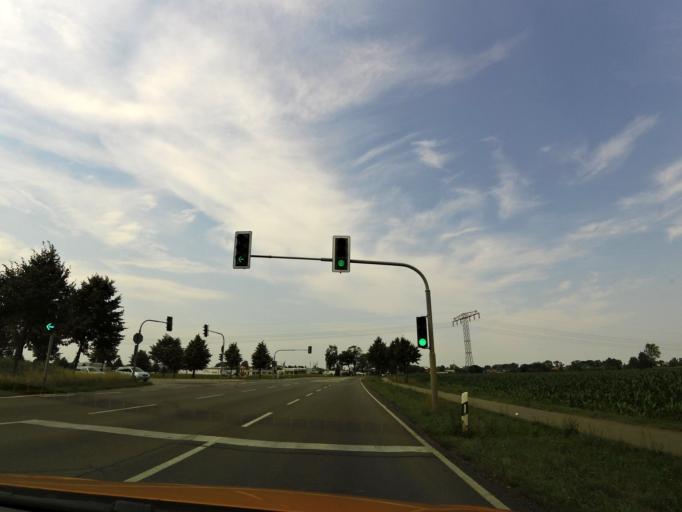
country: DE
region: Brandenburg
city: Kyritz
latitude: 52.9327
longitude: 12.4122
